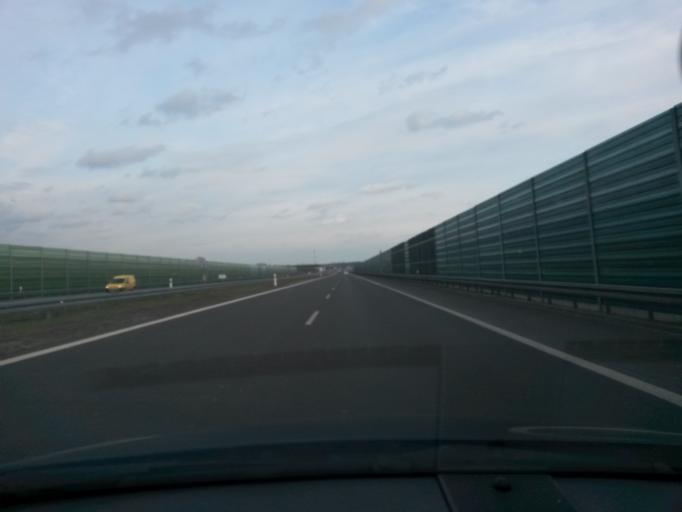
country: PL
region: Greater Poland Voivodeship
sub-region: Powiat kolski
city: Grzegorzew
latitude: 52.1207
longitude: 18.6973
